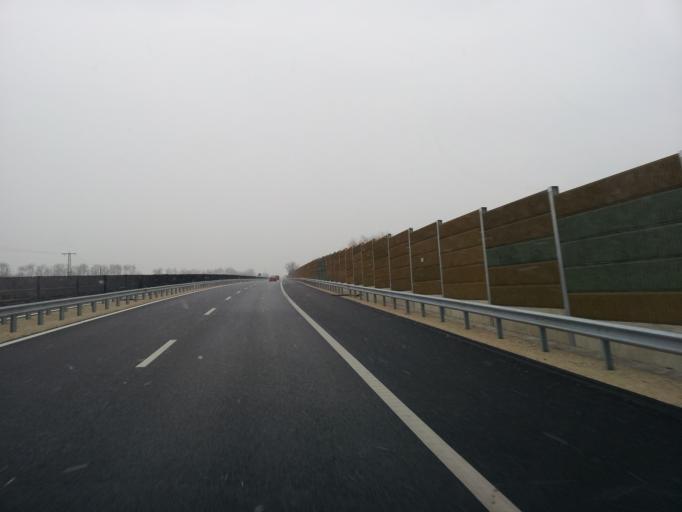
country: HU
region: Veszprem
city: Herend
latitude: 47.1325
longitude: 17.7392
